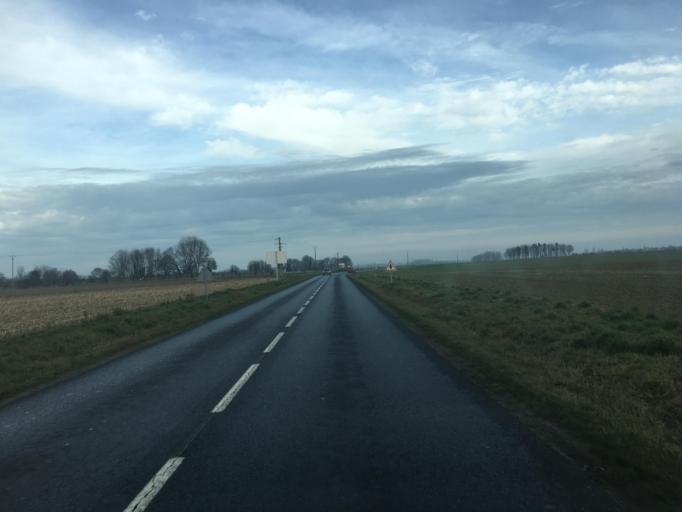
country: FR
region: Lower Normandy
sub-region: Departement du Calvados
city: Creully
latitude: 49.2357
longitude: -0.5779
